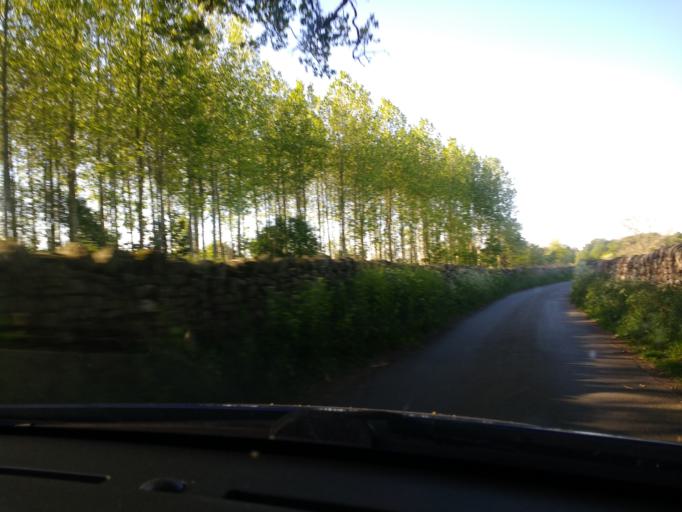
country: GB
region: England
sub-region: Cumbria
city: Appleby-in-Westmorland
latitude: 54.6717
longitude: -2.5930
